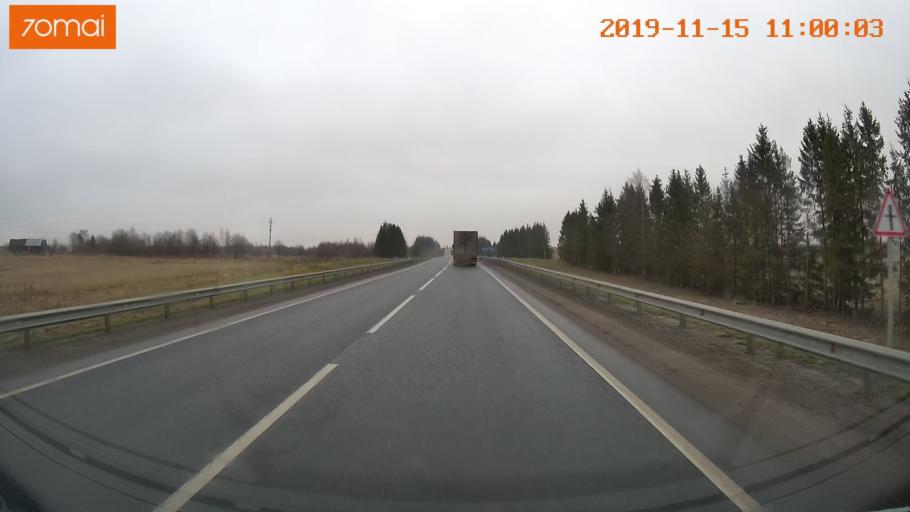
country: RU
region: Vologda
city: Chebsara
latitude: 59.1390
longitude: 38.8900
